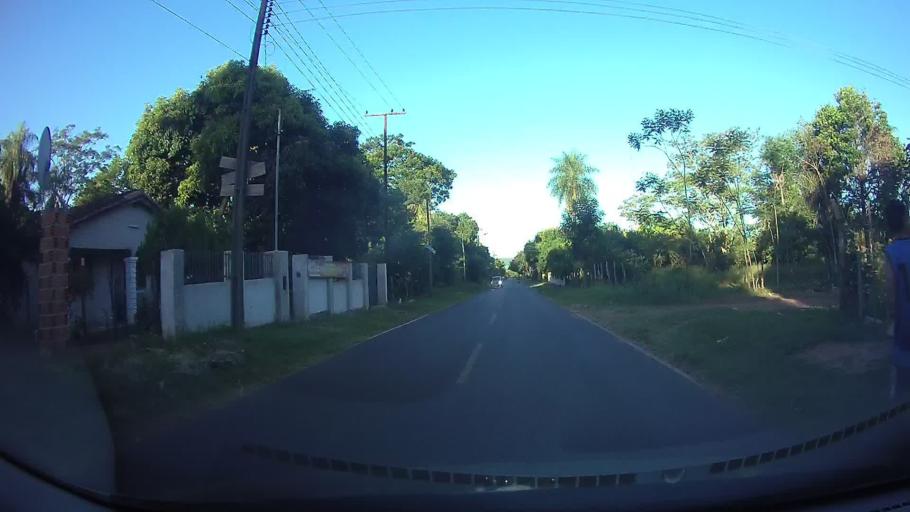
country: PY
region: Central
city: Aregua
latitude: -25.2845
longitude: -57.4009
